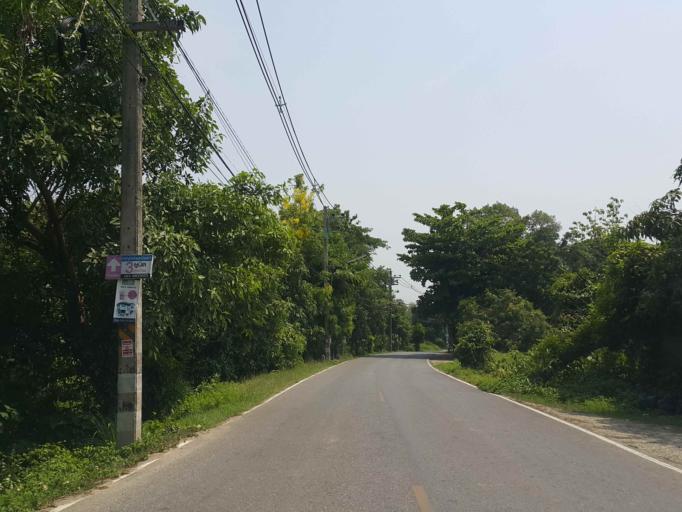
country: TH
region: Chiang Mai
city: San Sai
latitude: 18.8758
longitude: 98.9782
